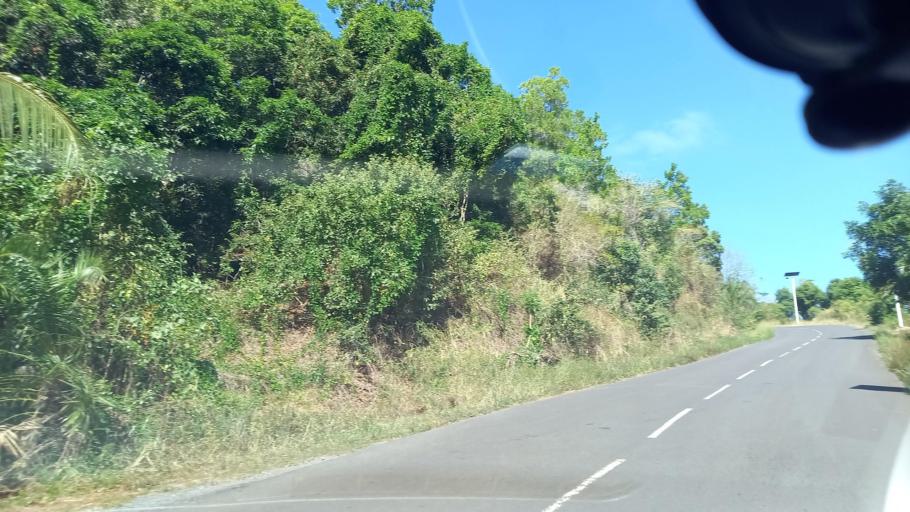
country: YT
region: Kani-Keli
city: Kani Keli
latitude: -12.9611
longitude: 45.1122
